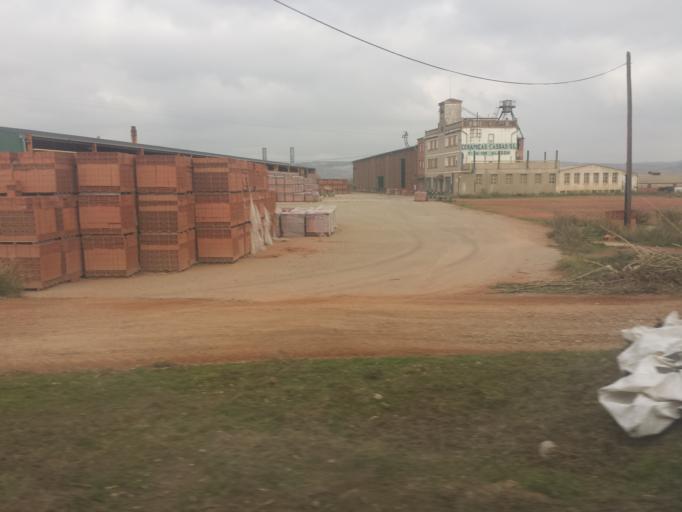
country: ES
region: Aragon
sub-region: Provincia de Zaragoza
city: Alagon
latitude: 41.7729
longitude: -1.1147
